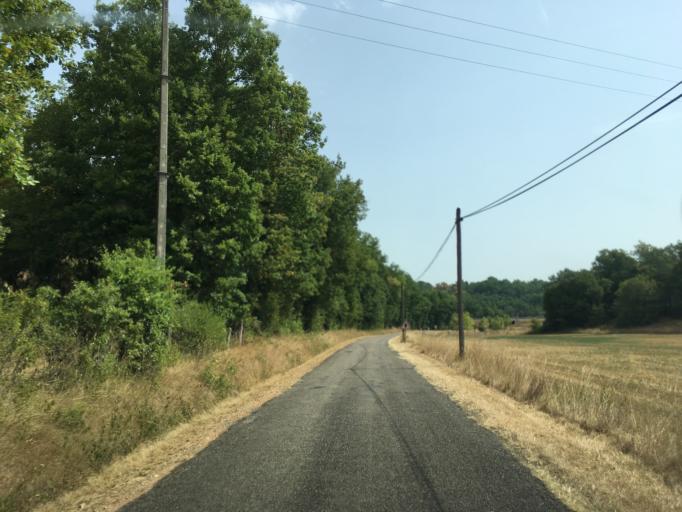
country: FR
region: Midi-Pyrenees
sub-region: Departement du Lot
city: Le Vigan
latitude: 44.7557
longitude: 1.5355
